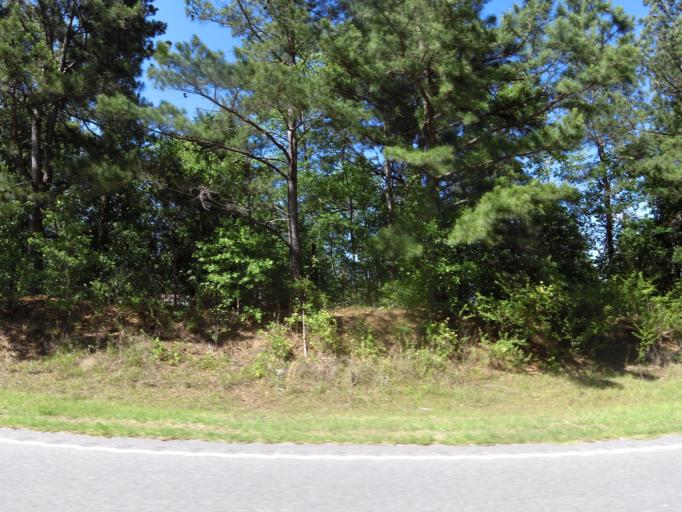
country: US
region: South Carolina
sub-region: Barnwell County
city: Williston
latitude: 33.3785
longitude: -81.3717
